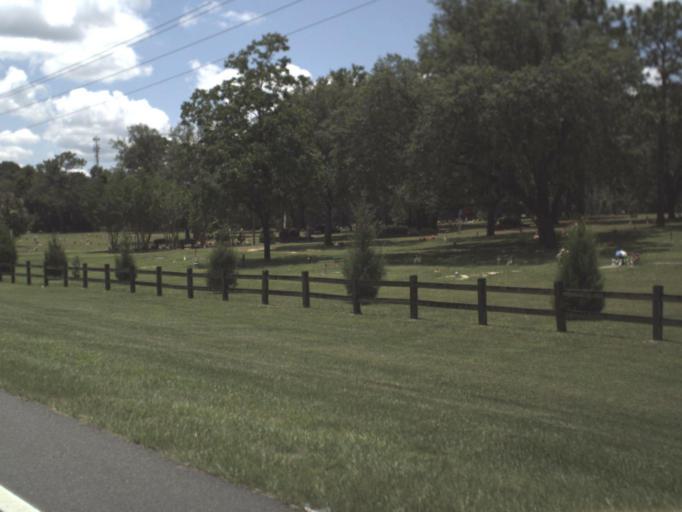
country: US
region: Florida
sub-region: Clay County
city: Keystone Heights
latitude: 29.7945
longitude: -82.0456
